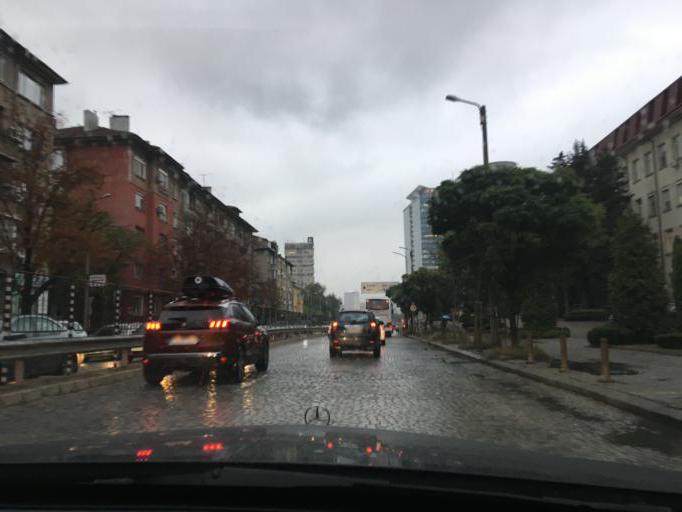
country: BG
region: Sofia-Capital
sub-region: Stolichna Obshtina
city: Sofia
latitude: 42.6857
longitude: 23.3120
